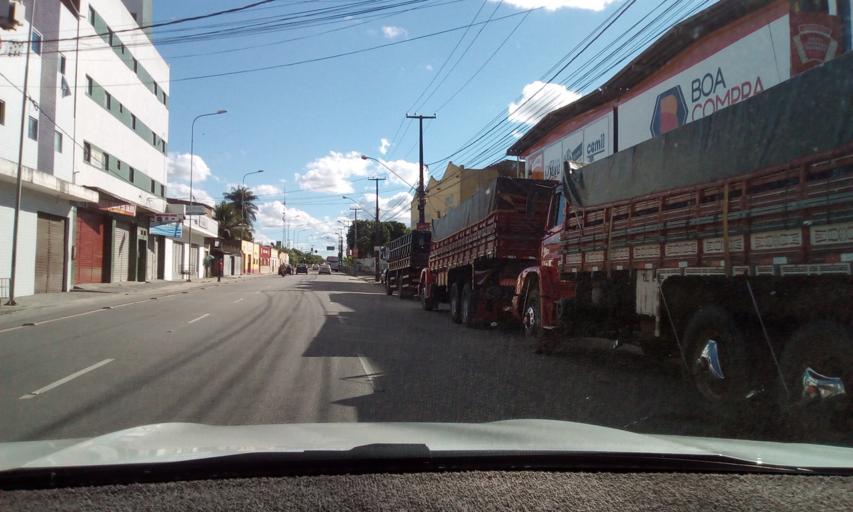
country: BR
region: Paraiba
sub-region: Campina Grande
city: Campina Grande
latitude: -7.2288
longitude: -35.8915
